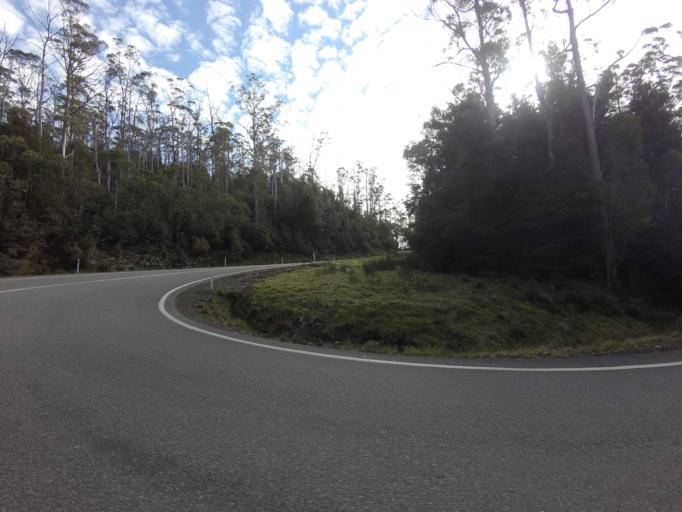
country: AU
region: Tasmania
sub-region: Meander Valley
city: Deloraine
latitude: -41.6980
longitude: 146.7280
